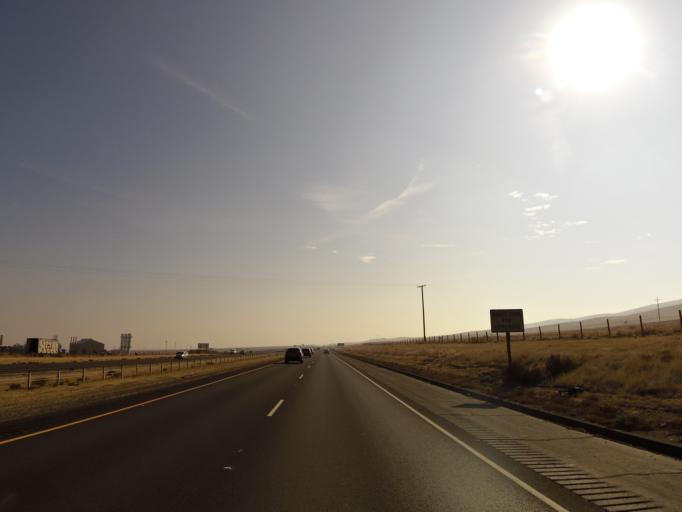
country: US
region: California
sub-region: Kings County
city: Avenal
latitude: 36.0717
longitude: -120.0939
